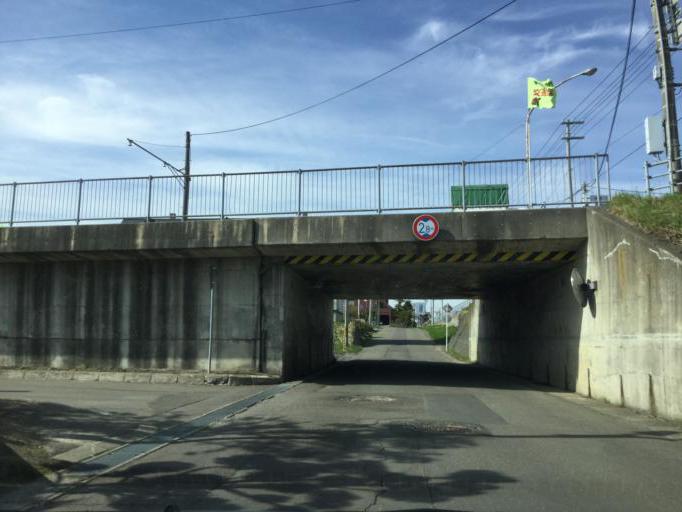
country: JP
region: Hokkaido
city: Iwamizawa
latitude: 43.2197
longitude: 141.7882
